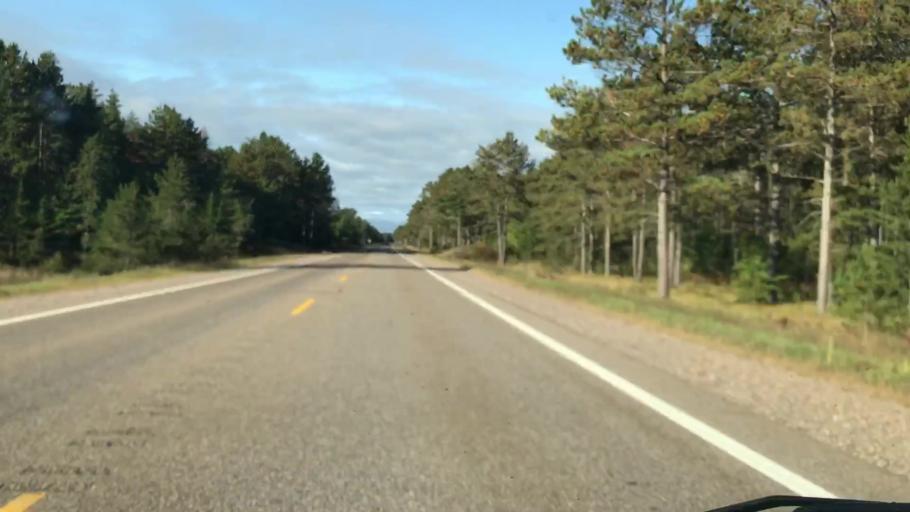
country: US
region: Michigan
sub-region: Mackinac County
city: Saint Ignace
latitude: 46.3545
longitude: -84.8986
